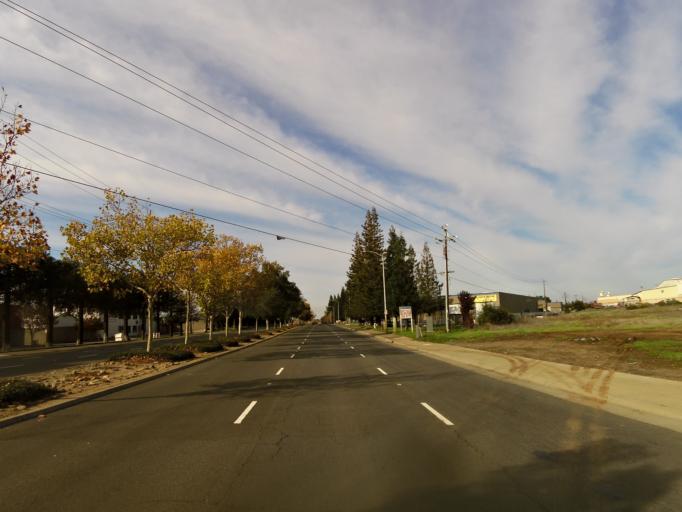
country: US
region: California
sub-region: Sacramento County
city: Rancho Cordova
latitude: 38.5735
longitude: -121.2569
